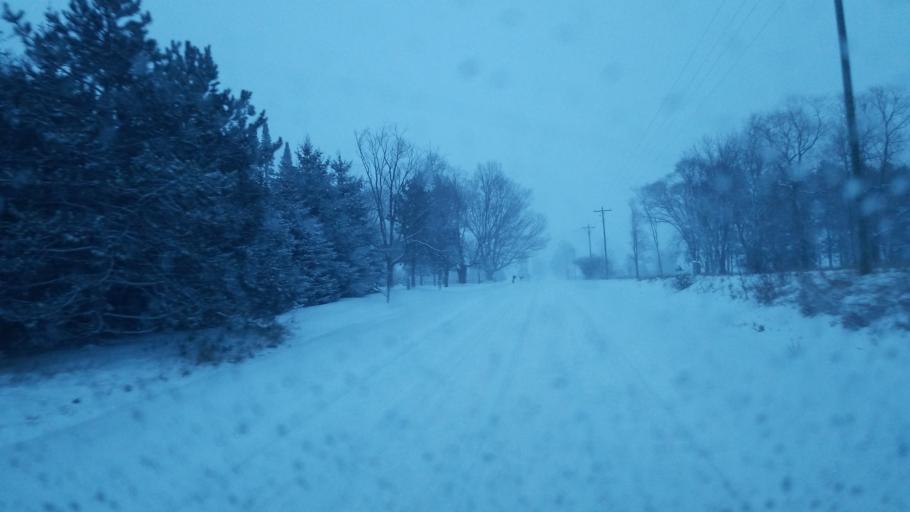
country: US
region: Michigan
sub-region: Osceola County
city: Reed City
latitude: 43.8218
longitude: -85.4082
